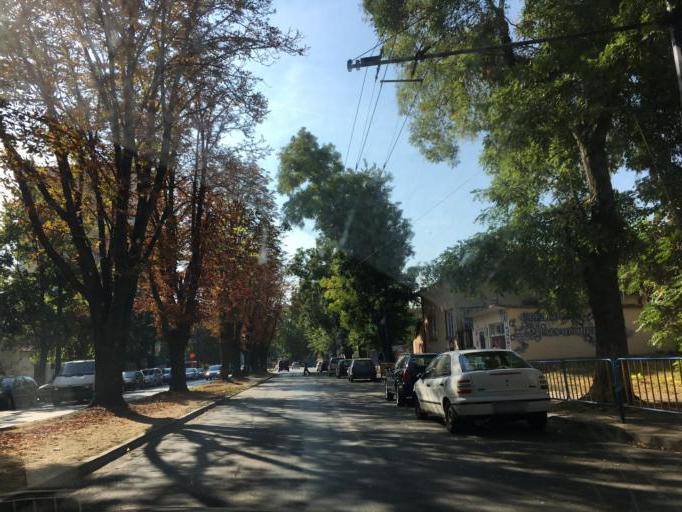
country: BG
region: Pazardzhik
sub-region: Obshtina Pazardzhik
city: Pazardzhik
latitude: 42.2008
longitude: 24.3324
